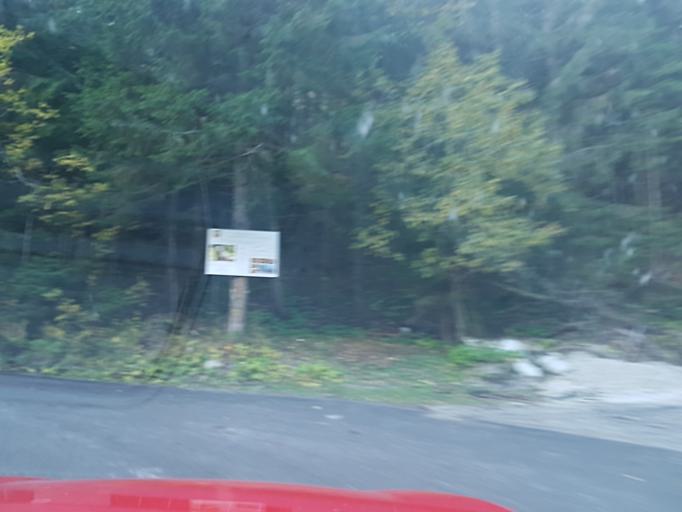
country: SK
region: Zilinsky
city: Ruzomberok
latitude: 48.9977
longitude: 19.2278
